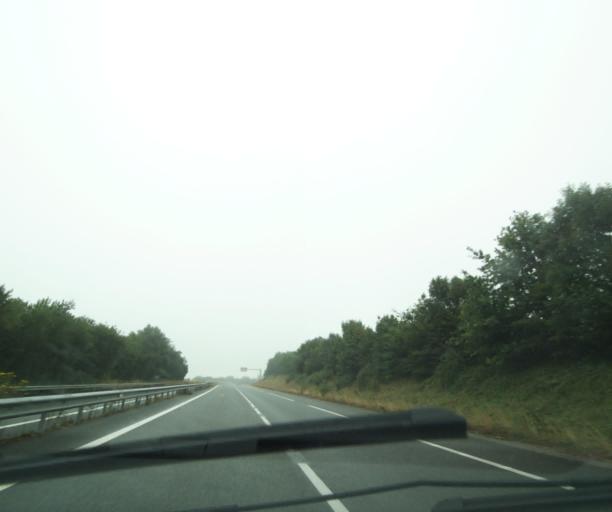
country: FR
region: Midi-Pyrenees
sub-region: Departement de l'Aveyron
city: Naucelle
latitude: 44.1394
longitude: 2.3125
